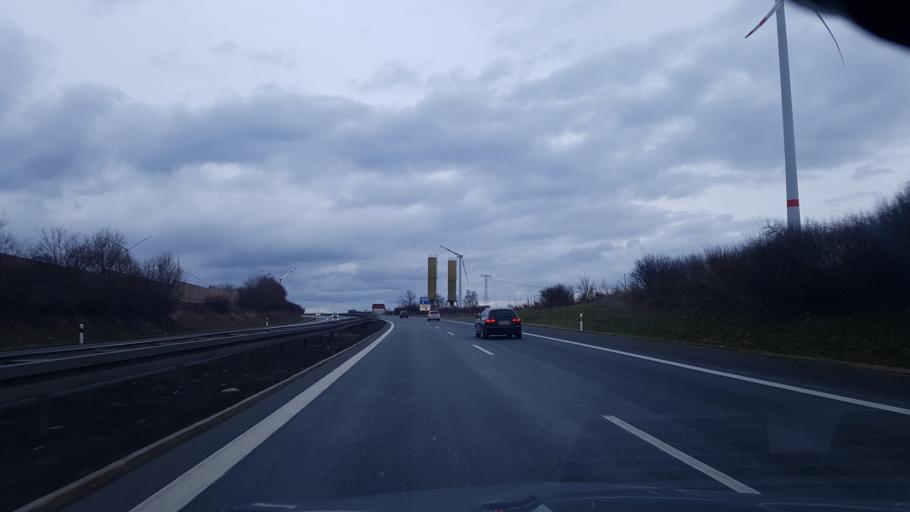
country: DE
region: Saxony
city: Reinsdorf
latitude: 50.6739
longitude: 12.5582
